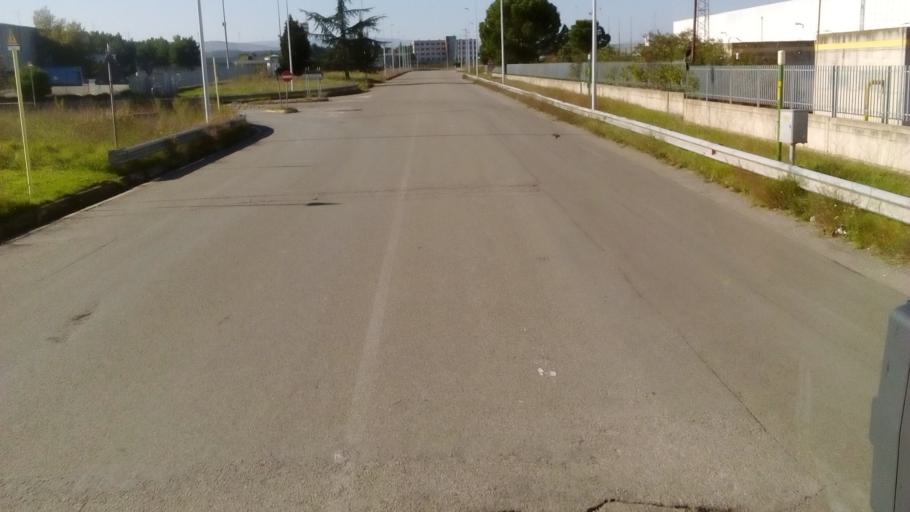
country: IT
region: Basilicate
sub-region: Provincia di Potenza
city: Melfi
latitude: 41.0761
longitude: 15.6808
